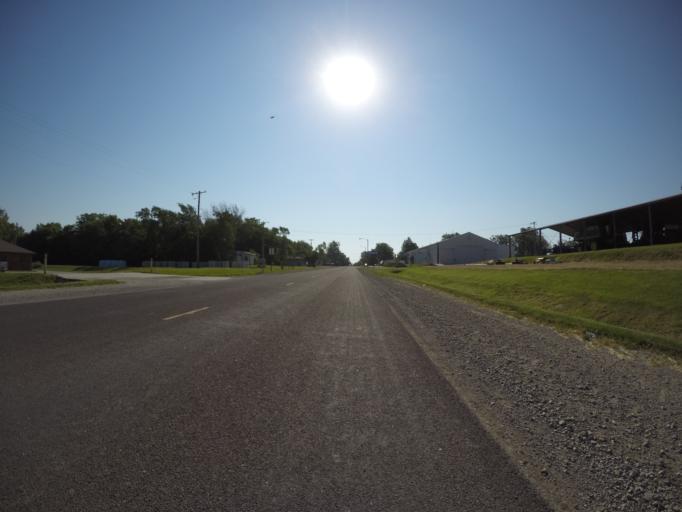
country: US
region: Kansas
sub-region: Brown County
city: Hiawatha
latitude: 39.8529
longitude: -95.5489
